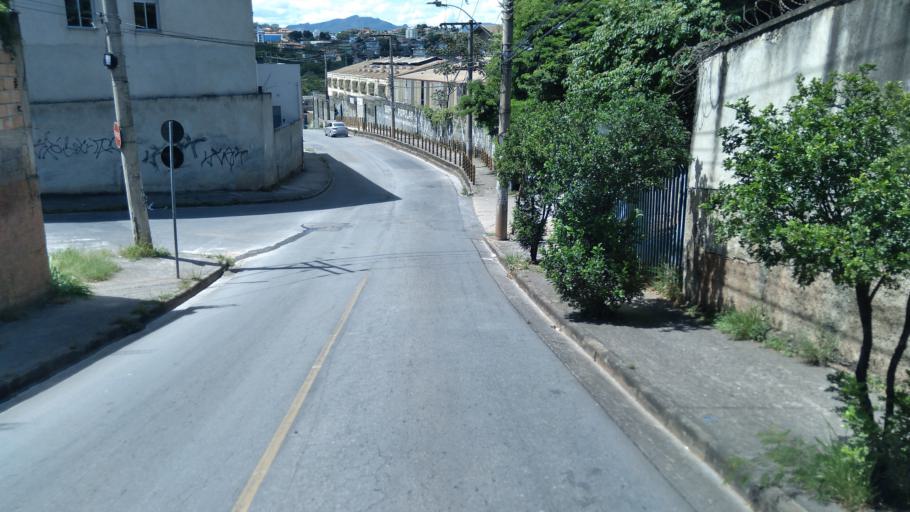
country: BR
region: Minas Gerais
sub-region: Belo Horizonte
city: Belo Horizonte
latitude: -19.8548
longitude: -43.8972
